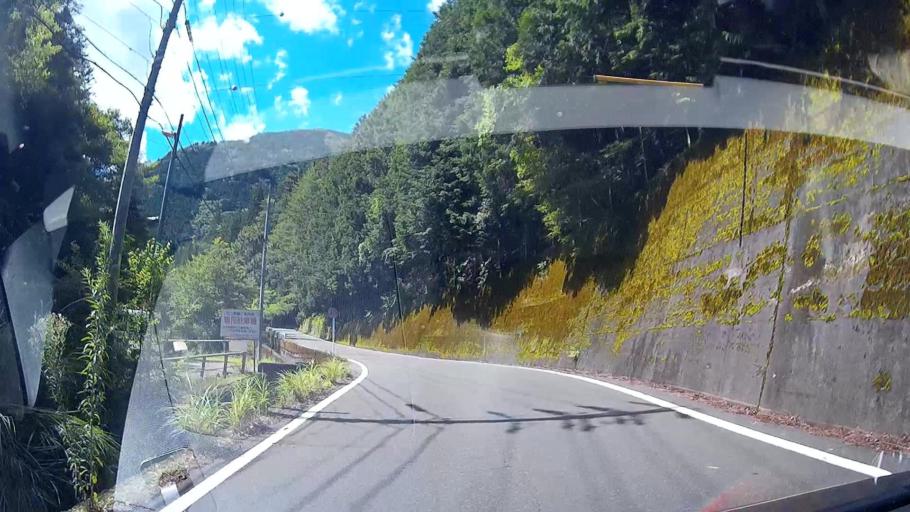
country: JP
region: Shizuoka
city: Shizuoka-shi
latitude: 35.2131
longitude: 138.2211
